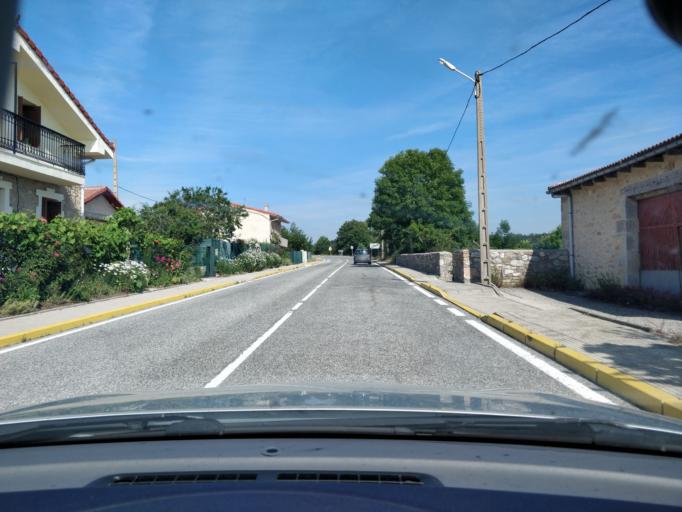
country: ES
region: Cantabria
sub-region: Provincia de Cantabria
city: San Martin de Elines
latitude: 42.9351
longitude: -3.7163
